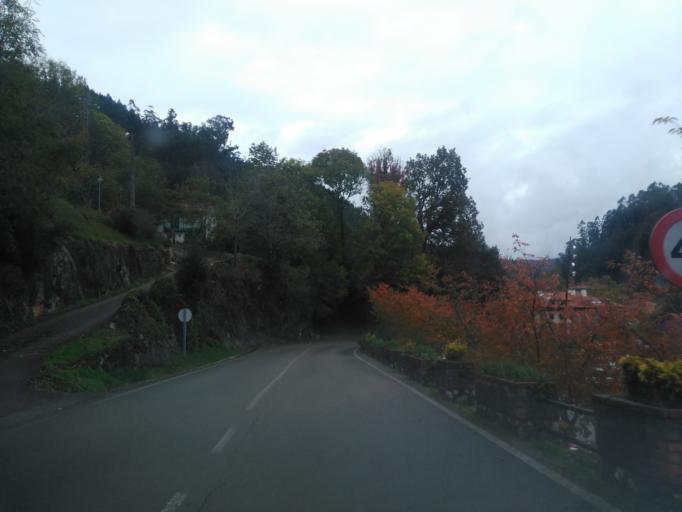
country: ES
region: Cantabria
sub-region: Provincia de Cantabria
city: Puente Viesgo
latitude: 43.2979
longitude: -3.9683
